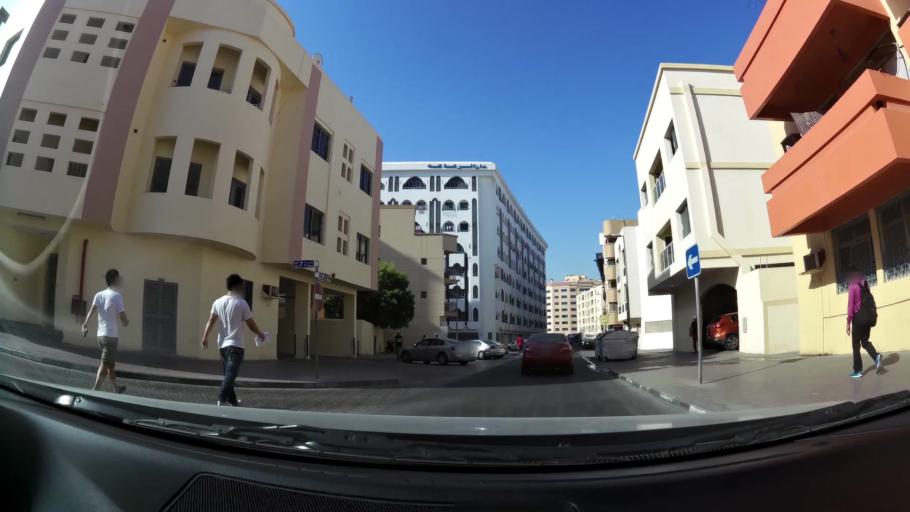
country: AE
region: Ash Shariqah
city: Sharjah
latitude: 25.2585
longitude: 55.2868
